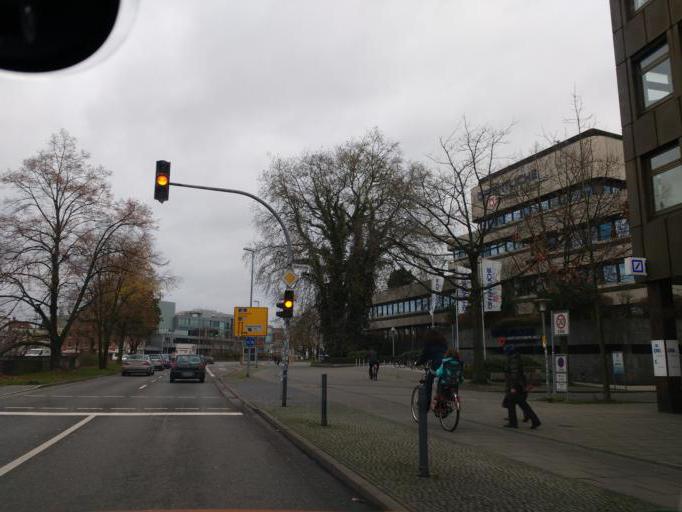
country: DE
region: Lower Saxony
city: Oldenburg
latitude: 53.1425
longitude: 8.2154
